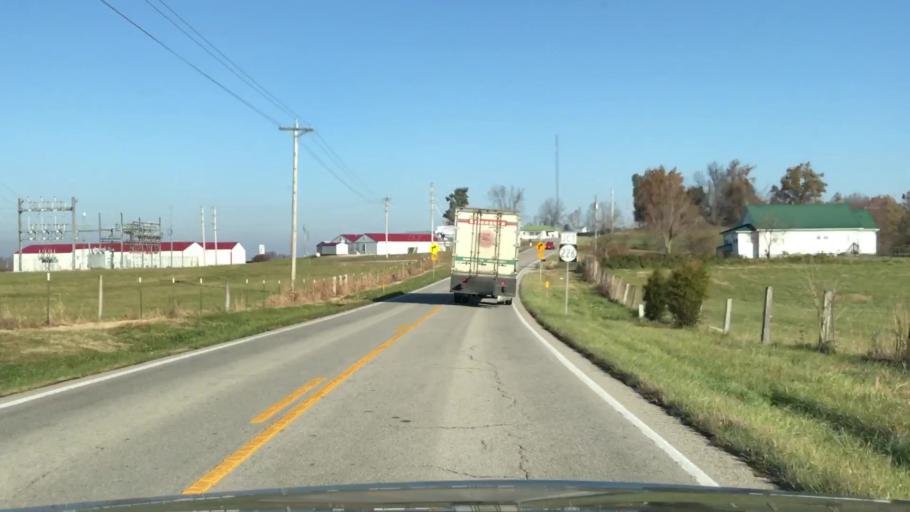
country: US
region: Kentucky
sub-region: Grayson County
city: Leitchfield
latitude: 37.4015
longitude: -86.2374
